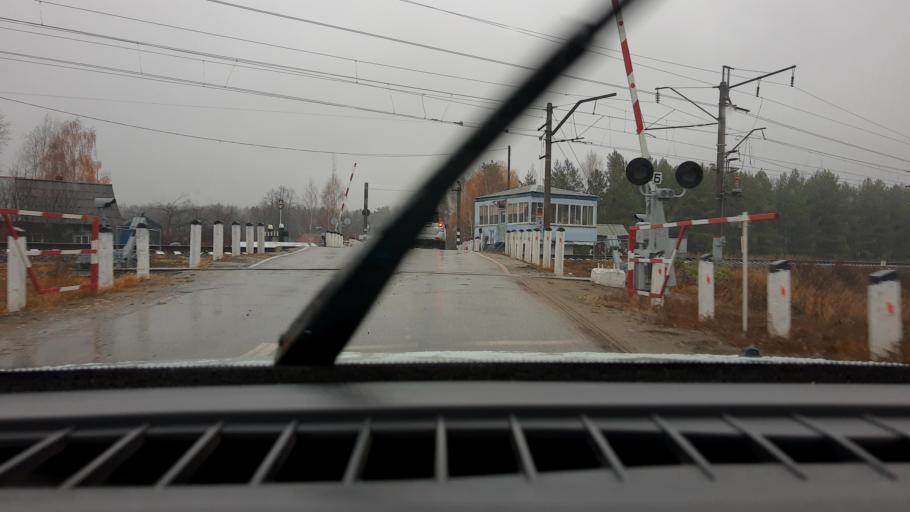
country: RU
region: Nizjnij Novgorod
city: Linda
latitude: 56.6848
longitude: 44.2021
